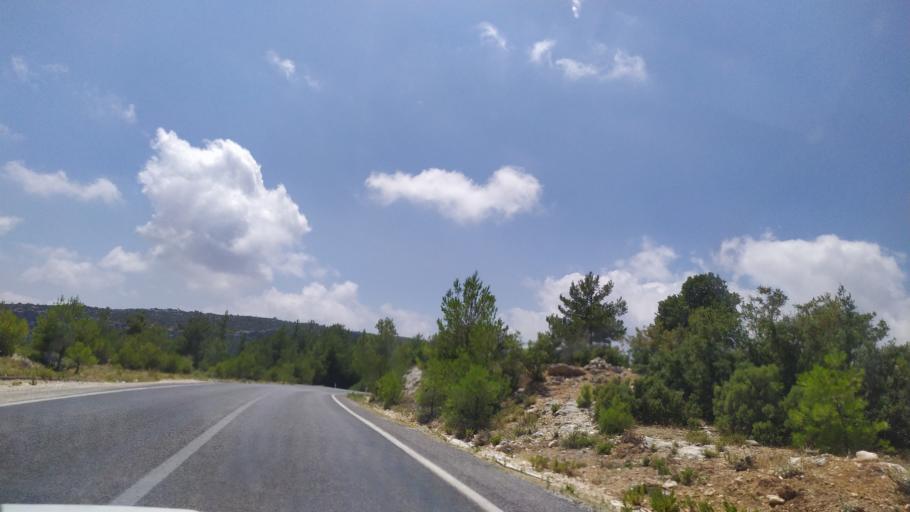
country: TR
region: Mersin
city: Gulnar
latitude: 36.2784
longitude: 33.3886
